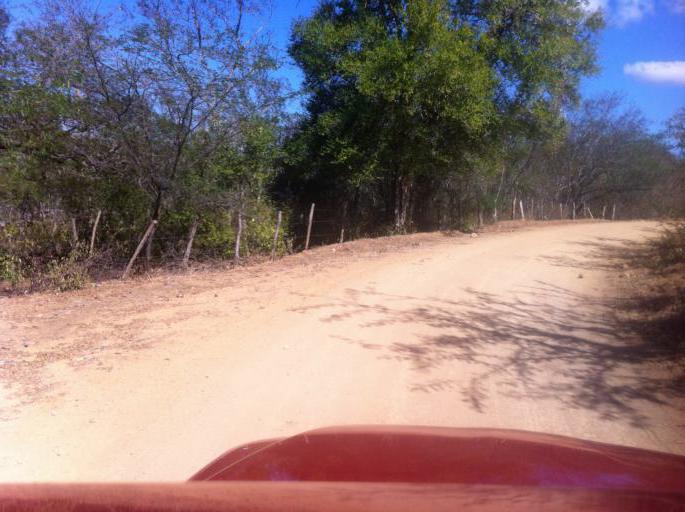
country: NI
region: Carazo
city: Santa Teresa
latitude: 11.6183
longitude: -86.3218
